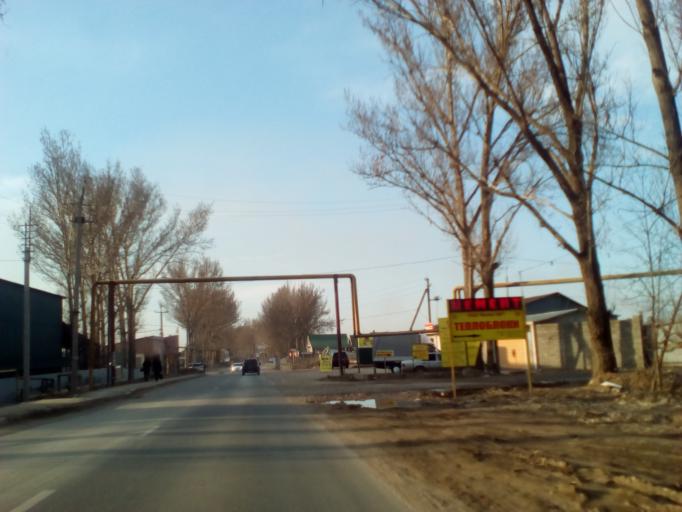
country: KZ
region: Almaty Oblysy
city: Burunday
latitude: 43.2482
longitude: 76.7849
